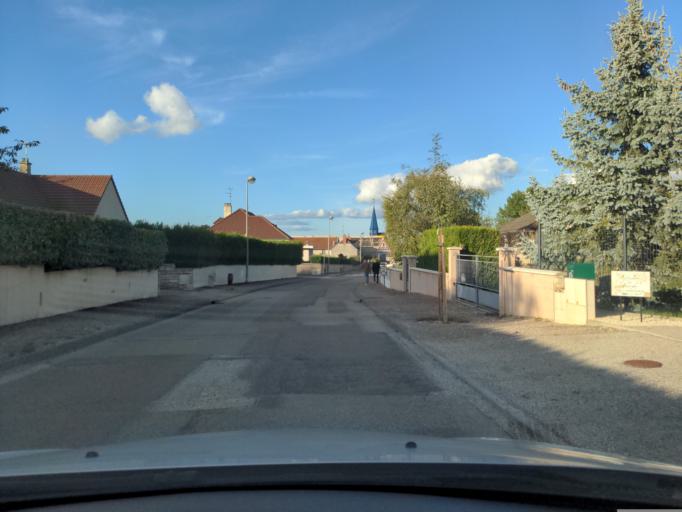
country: FR
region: Bourgogne
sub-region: Departement de la Cote-d'Or
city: Ruffey-les-Echirey
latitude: 47.3779
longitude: 5.0693
